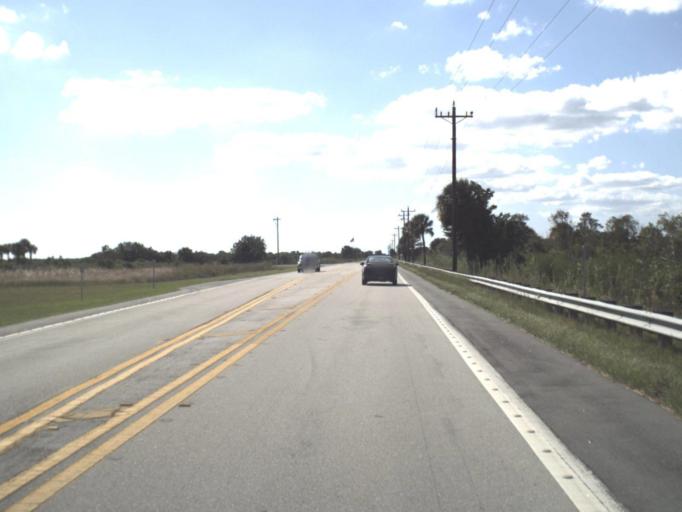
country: US
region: Florida
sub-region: Collier County
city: Marco
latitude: 25.9014
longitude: -81.3244
